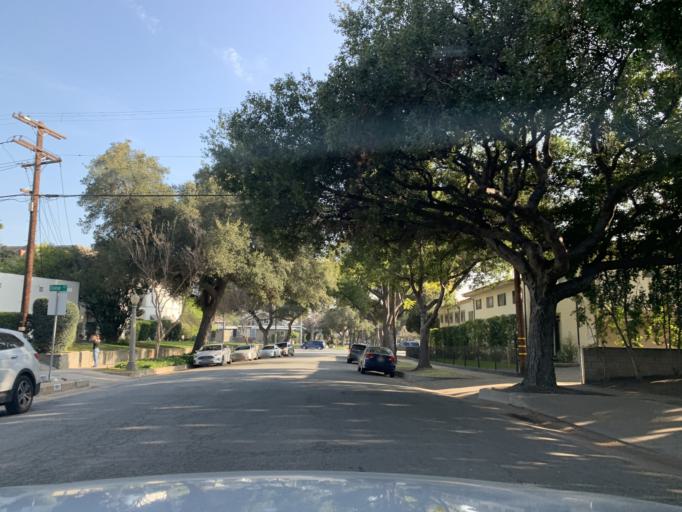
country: US
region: California
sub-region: Los Angeles County
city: Altadena
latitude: 34.1699
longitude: -118.1258
